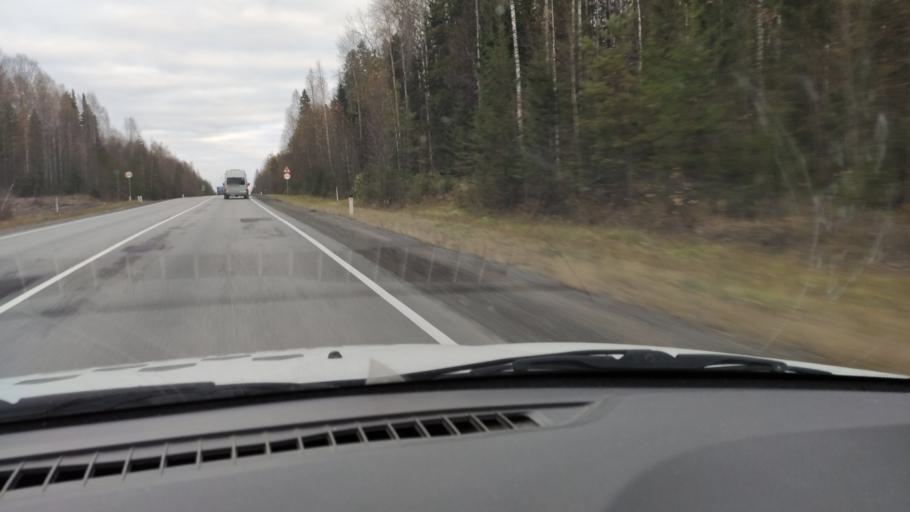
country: RU
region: Kirov
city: Chernaya Kholunitsa
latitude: 58.8587
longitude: 51.6358
